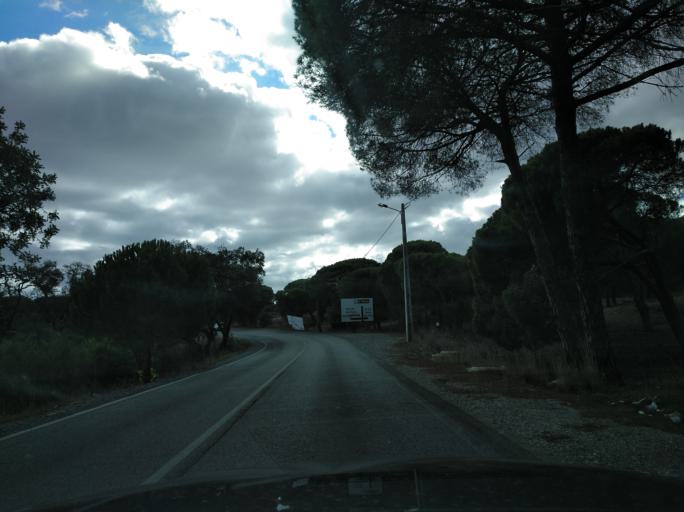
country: PT
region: Faro
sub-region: Vila Real de Santo Antonio
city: Monte Gordo
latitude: 37.1862
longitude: -7.4845
